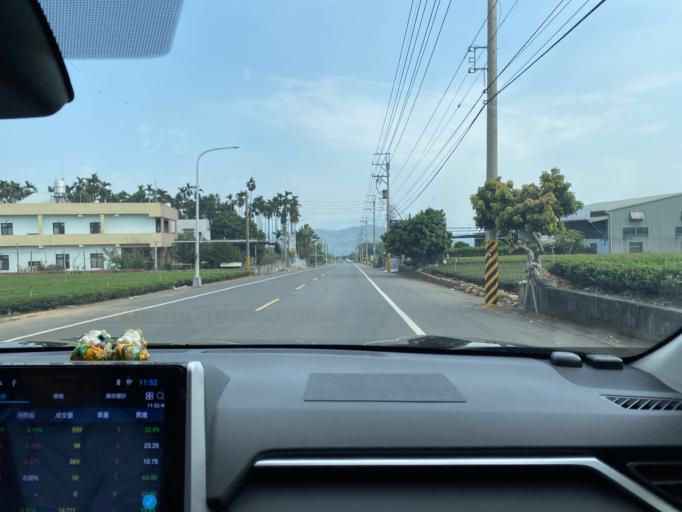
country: TW
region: Taiwan
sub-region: Nantou
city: Nantou
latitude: 23.8374
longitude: 120.6690
